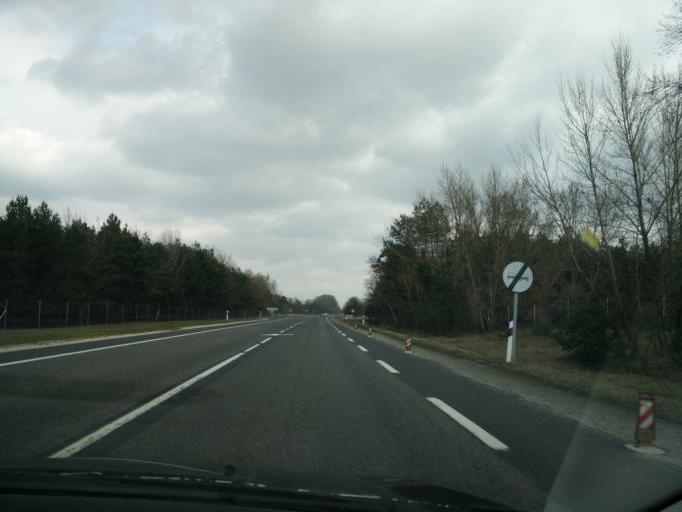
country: HU
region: Gyor-Moson-Sopron
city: Toltestava
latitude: 47.7123
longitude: 17.7402
